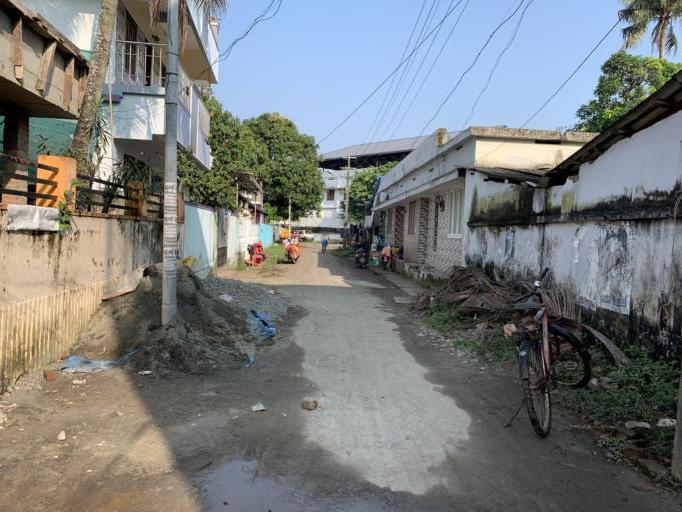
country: IN
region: Kerala
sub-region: Ernakulam
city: Cochin
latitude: 9.9598
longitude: 76.2511
